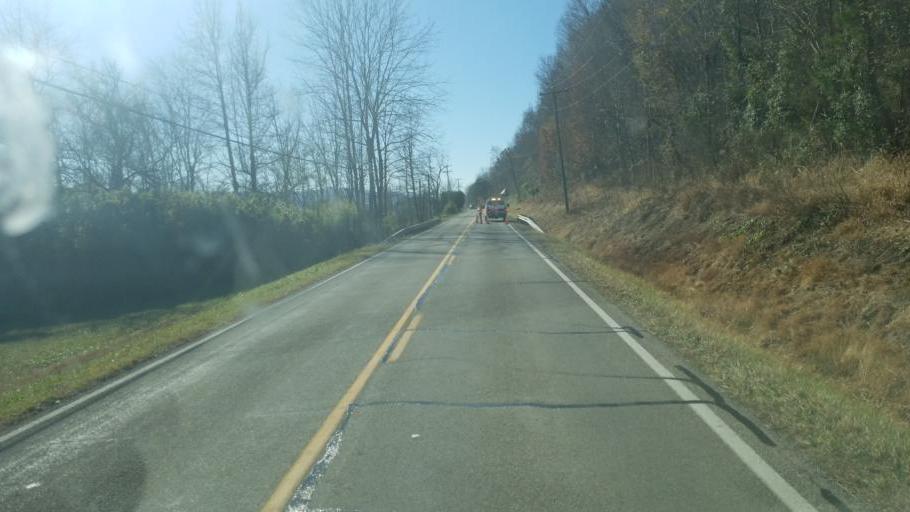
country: US
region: Ohio
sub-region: Scioto County
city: West Portsmouth
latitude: 38.6424
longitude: -83.1411
